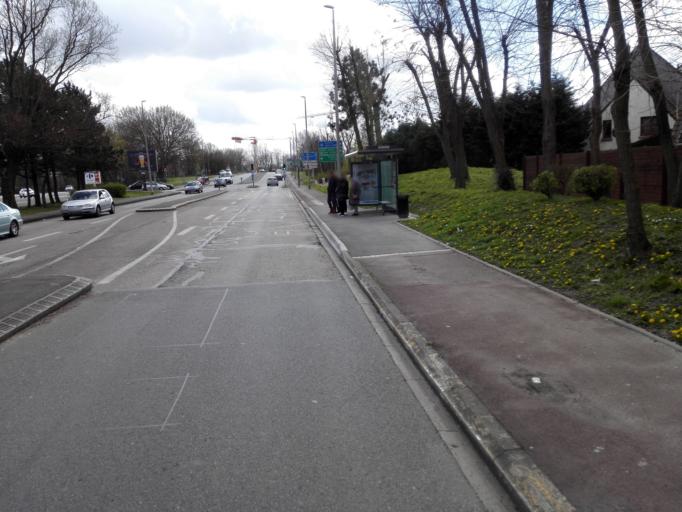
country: FR
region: Nord-Pas-de-Calais
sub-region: Departement du Nord
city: Saint-Pol-sur-Mer
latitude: 51.0250
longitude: 2.3332
